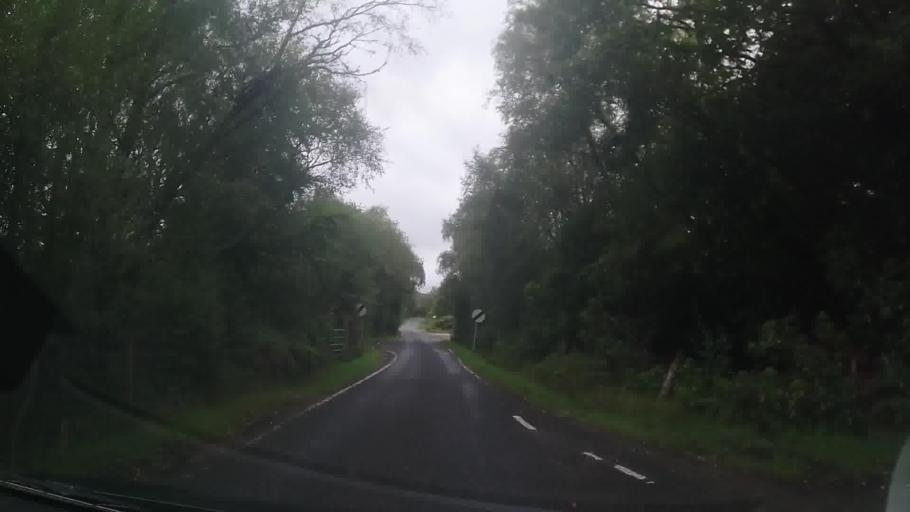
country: GB
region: Scotland
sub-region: Argyll and Bute
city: Isle Of Mull
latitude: 56.7116
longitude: -5.7798
